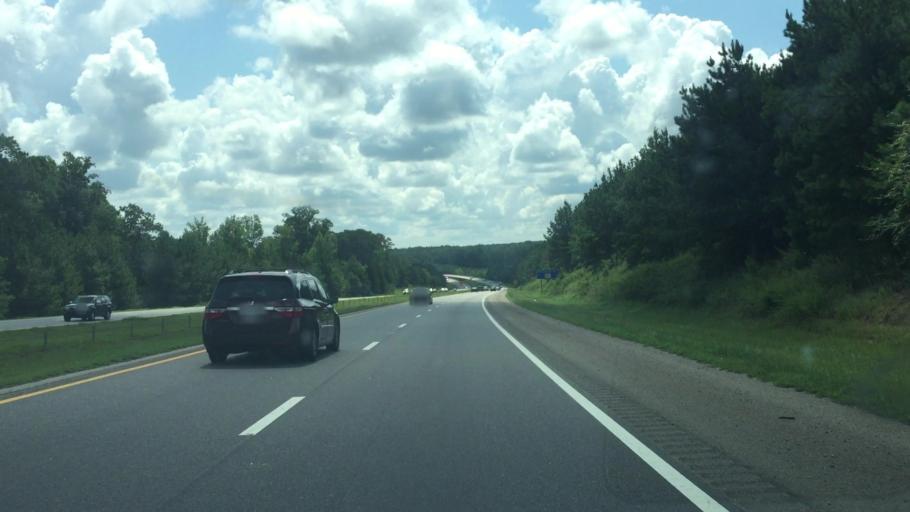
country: US
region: North Carolina
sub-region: Richmond County
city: Cordova
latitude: 34.9273
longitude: -79.8217
